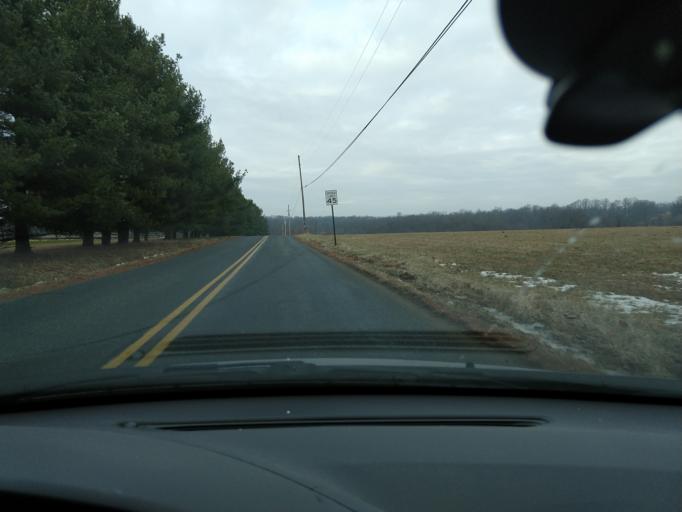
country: US
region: Pennsylvania
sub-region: Berks County
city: Amity Gardens
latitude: 40.2375
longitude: -75.7526
